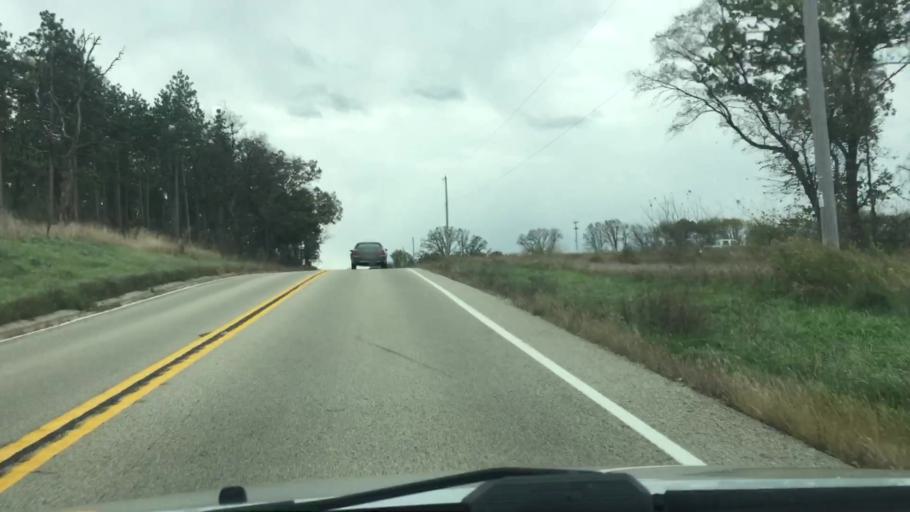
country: US
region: Wisconsin
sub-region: Waukesha County
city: Eagle
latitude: 42.9102
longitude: -88.4738
